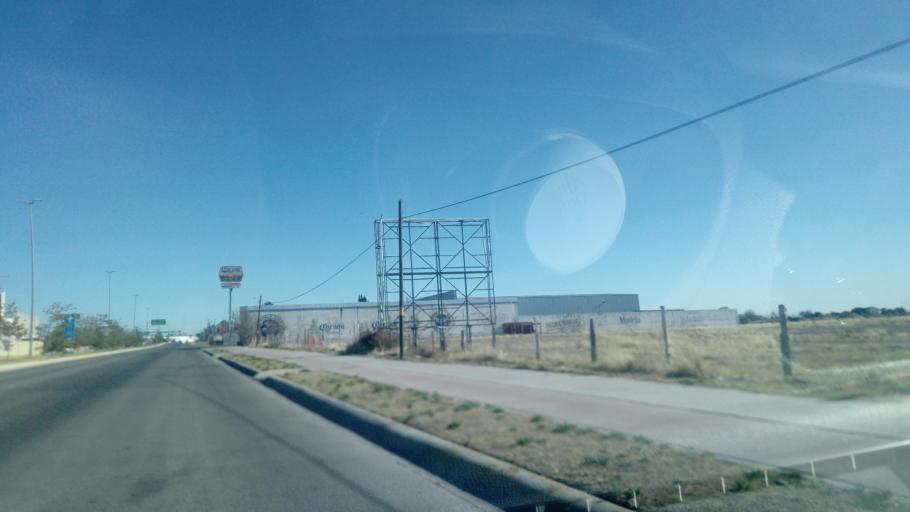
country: MX
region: Durango
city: Victoria de Durango
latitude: 24.0874
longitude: -104.5817
